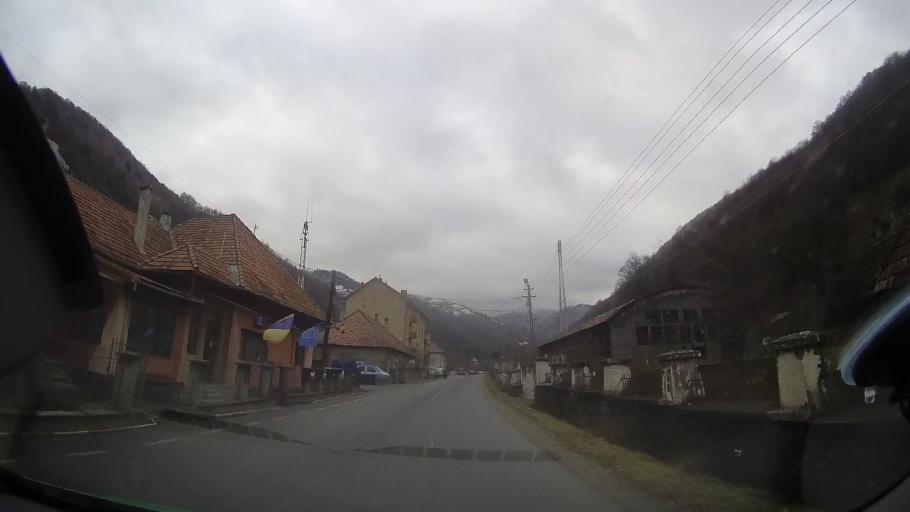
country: RO
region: Cluj
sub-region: Comuna Maguri-Racatau
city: Maguri-Racatau
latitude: 46.6480
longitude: 23.1968
